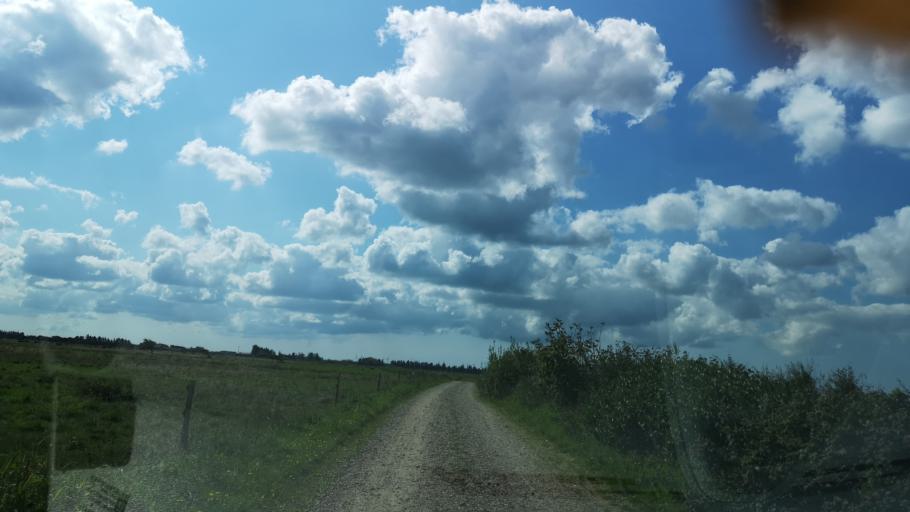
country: DK
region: Central Jutland
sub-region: Ringkobing-Skjern Kommune
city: Skjern
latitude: 55.9117
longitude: 8.4034
